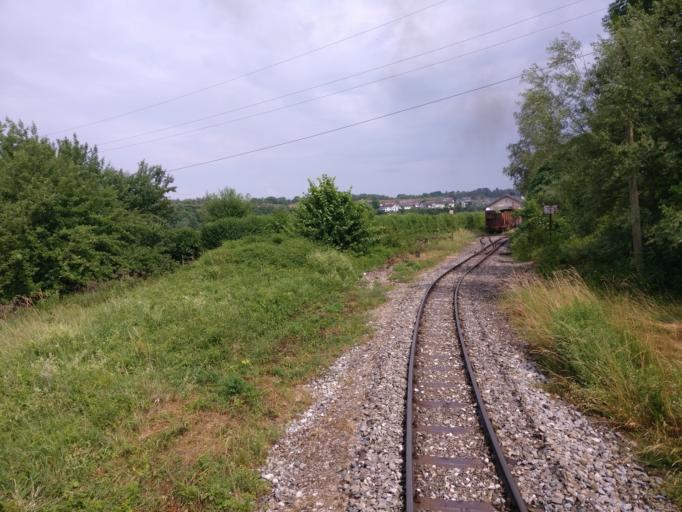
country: AT
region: Upper Austria
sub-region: Politischer Bezirk Steyr-Land
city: Sierning
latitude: 48.0392
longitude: 14.3332
